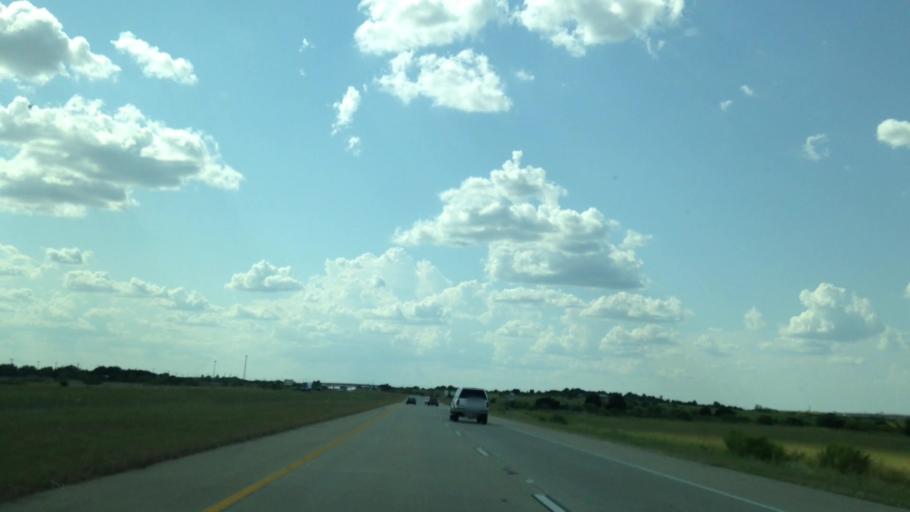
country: US
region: Texas
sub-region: Travis County
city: Onion Creek
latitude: 30.0870
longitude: -97.7420
